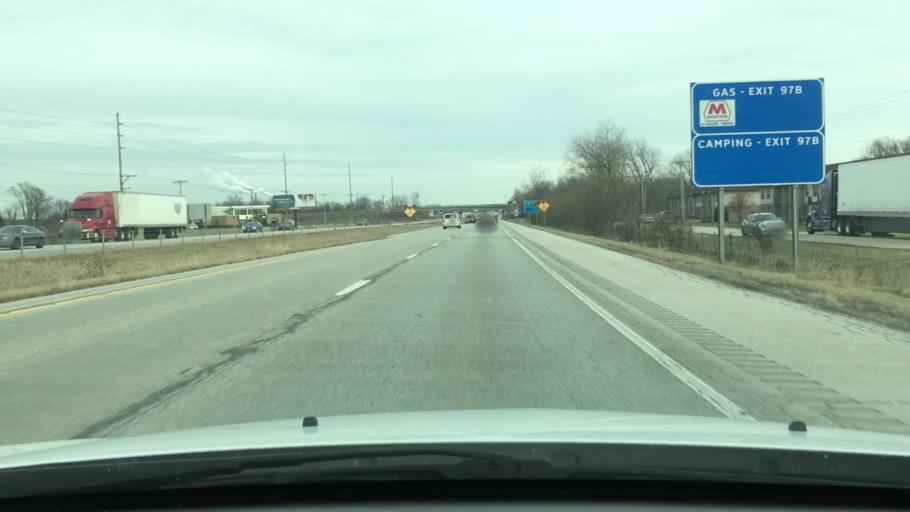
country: US
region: Illinois
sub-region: Sangamon County
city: Southern View
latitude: 39.7424
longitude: -89.6586
